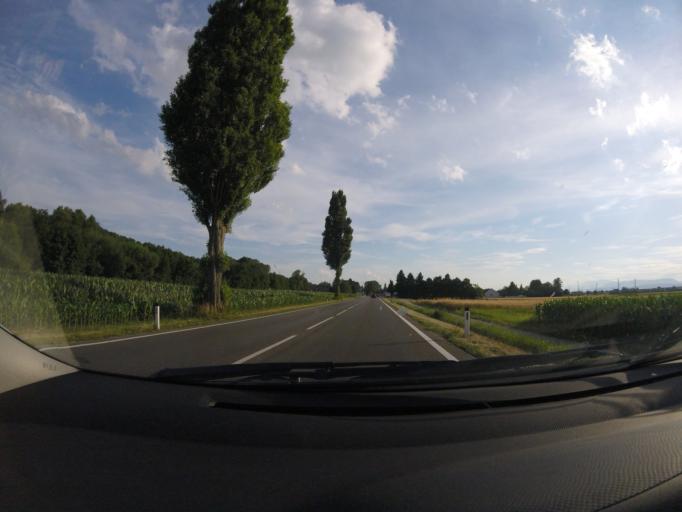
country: AT
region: Lower Austria
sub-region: Politischer Bezirk Wiener Neustadt
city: Zillingdorf
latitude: 47.8628
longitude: 16.3261
